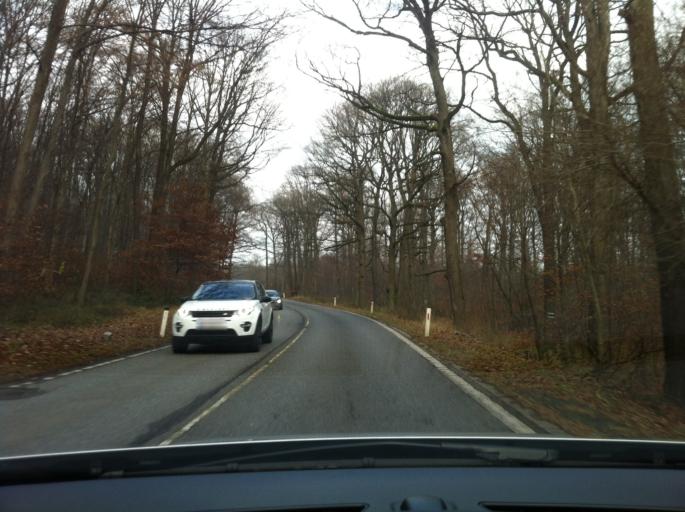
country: AT
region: Lower Austria
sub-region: Politischer Bezirk Wien-Umgebung
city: Purkersdorf
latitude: 48.2249
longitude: 16.2547
